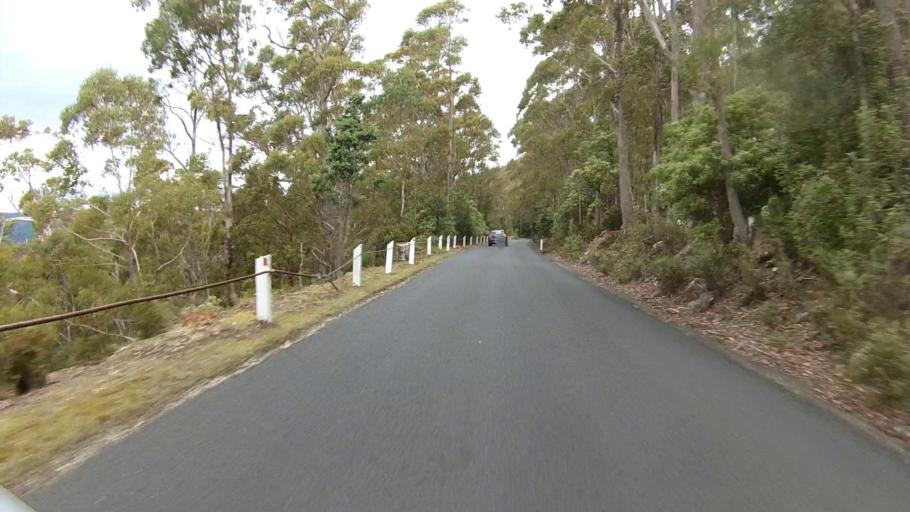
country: AU
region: Tasmania
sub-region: Glenorchy
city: West Moonah
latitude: -42.9097
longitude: 147.2439
